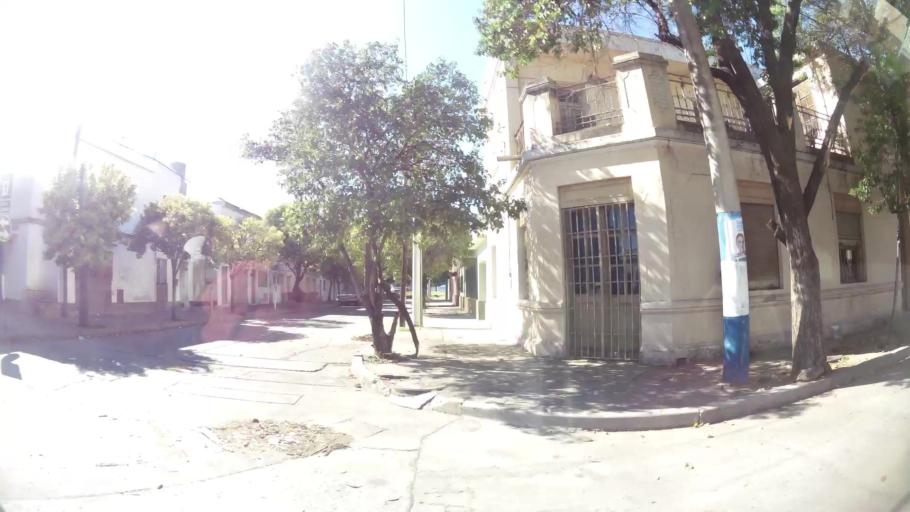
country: AR
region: Cordoba
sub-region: Departamento de Capital
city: Cordoba
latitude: -31.4398
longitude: -64.1601
